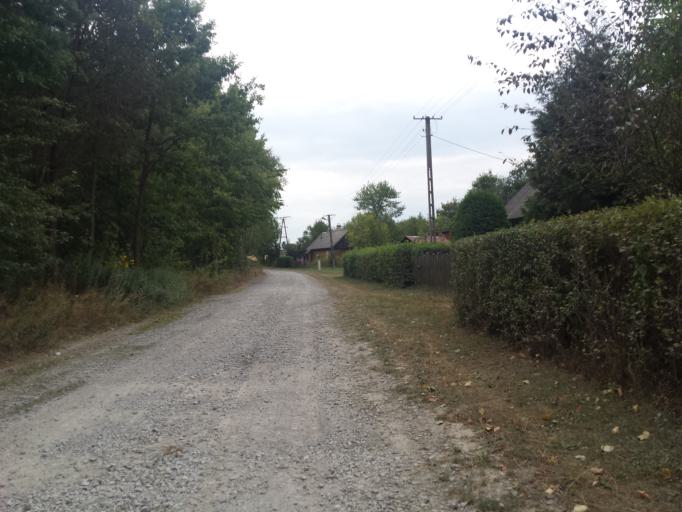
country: PL
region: Swietokrzyskie
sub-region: Powiat staszowski
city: Staszow
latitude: 50.6662
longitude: 21.1522
